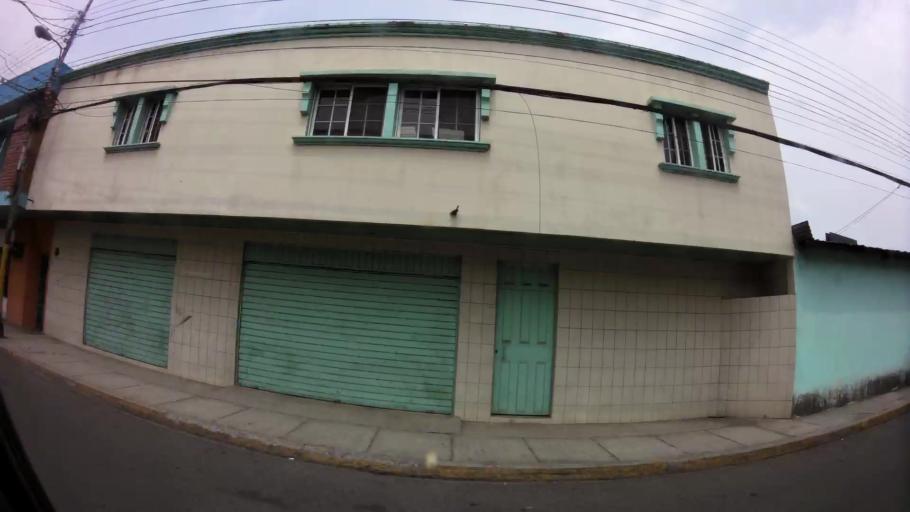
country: HN
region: Francisco Morazan
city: Tegucigalpa
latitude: 14.0969
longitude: -87.2064
